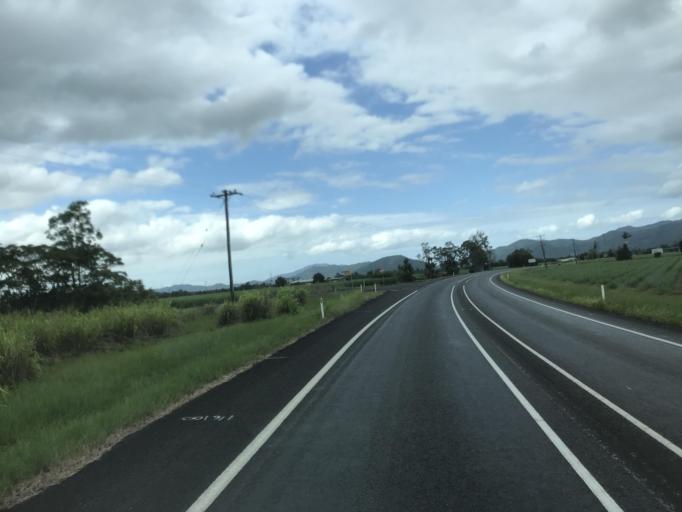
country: AU
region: Queensland
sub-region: Cassowary Coast
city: Innisfail
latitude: -17.7812
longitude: 146.0277
